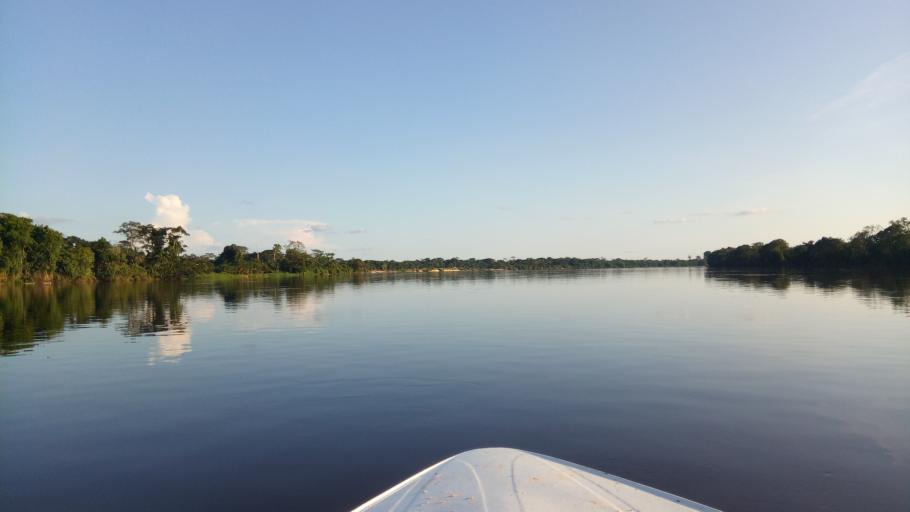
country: CD
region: Eastern Province
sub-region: Sous-Region de la Tshopo
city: Yangambi
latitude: 0.1589
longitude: 24.0522
